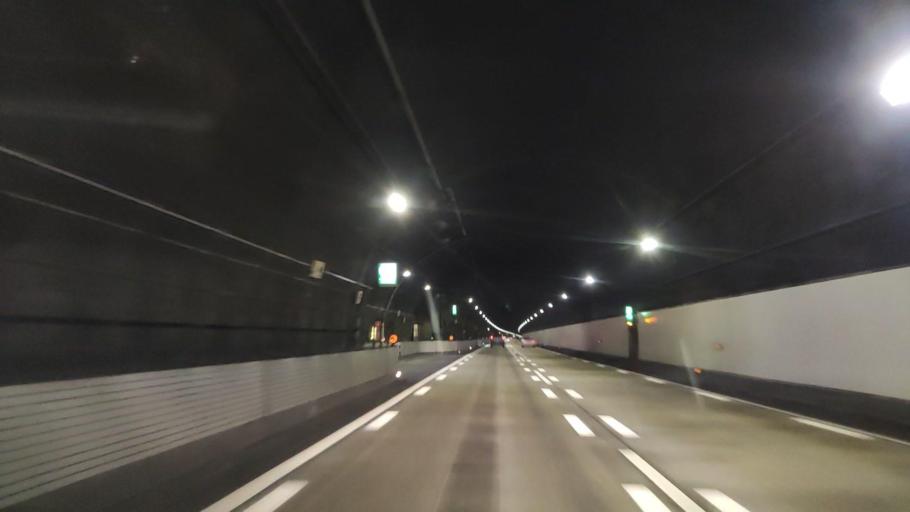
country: JP
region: Hiroshima
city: Fukuyama
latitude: 34.5012
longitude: 133.3236
